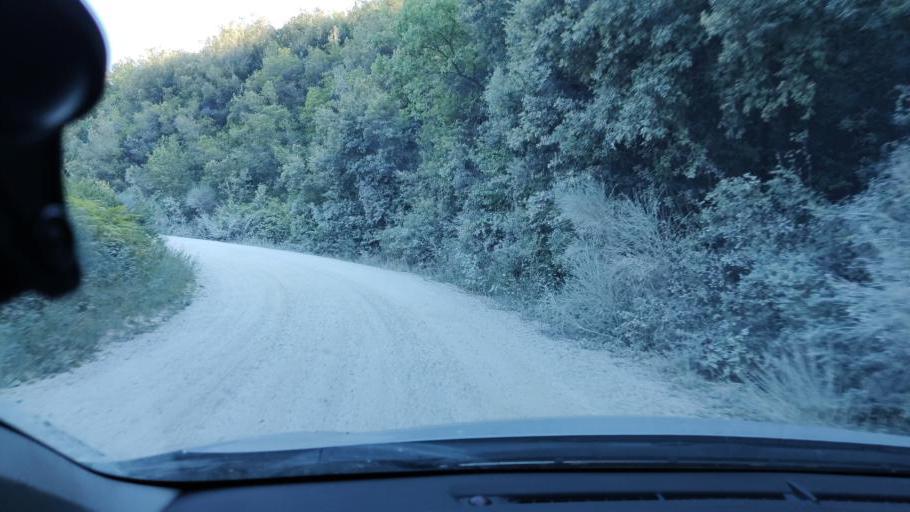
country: IT
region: Umbria
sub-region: Provincia di Terni
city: Amelia
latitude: 42.5400
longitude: 12.3828
